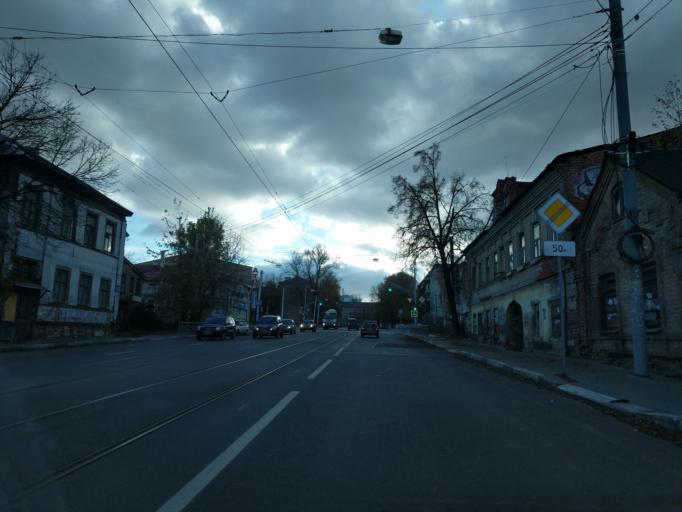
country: RU
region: Nizjnij Novgorod
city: Nizhniy Novgorod
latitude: 56.3112
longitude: 43.9845
